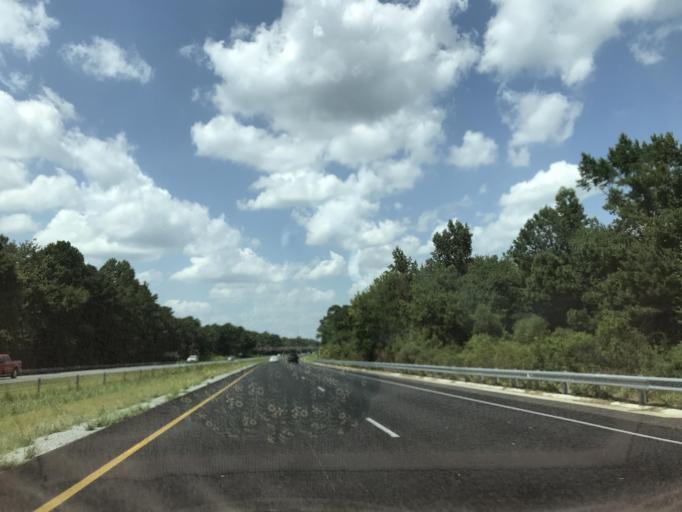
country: US
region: North Carolina
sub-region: Duplin County
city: Warsaw
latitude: 34.9334
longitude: -78.0462
